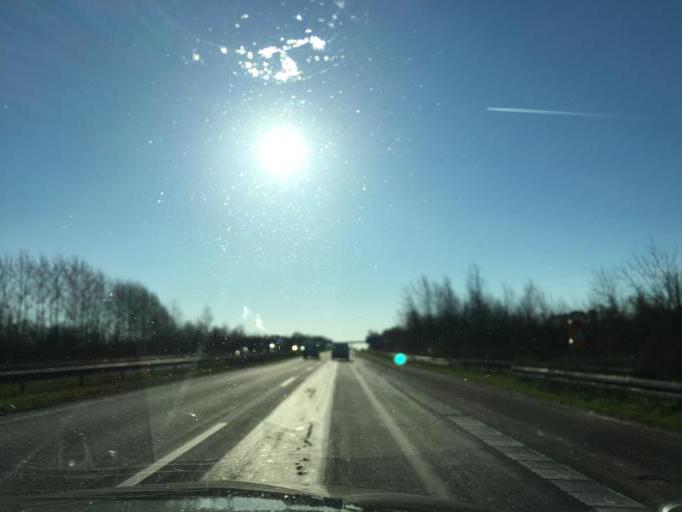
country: DK
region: South Denmark
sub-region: Assens Kommune
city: Vissenbjerg
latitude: 55.4067
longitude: 10.1329
